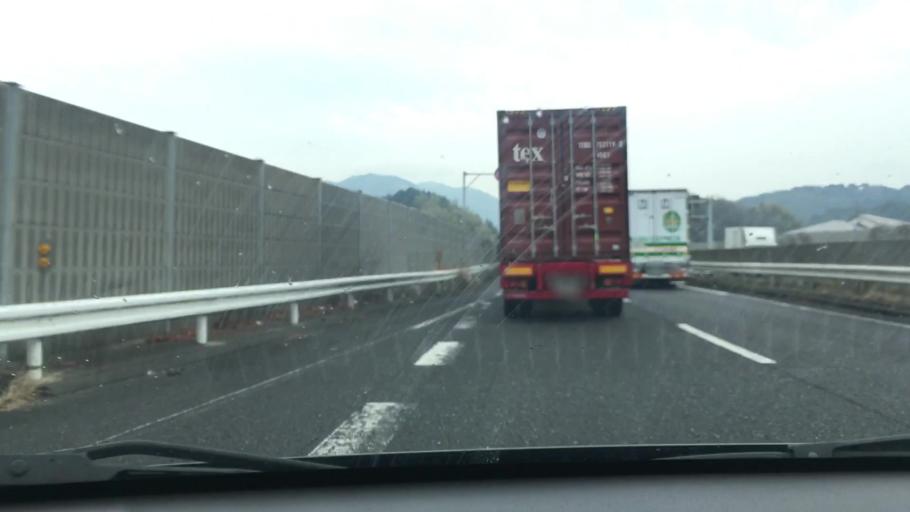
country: JP
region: Mie
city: Ueno-ebisumachi
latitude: 34.8321
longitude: 136.2401
